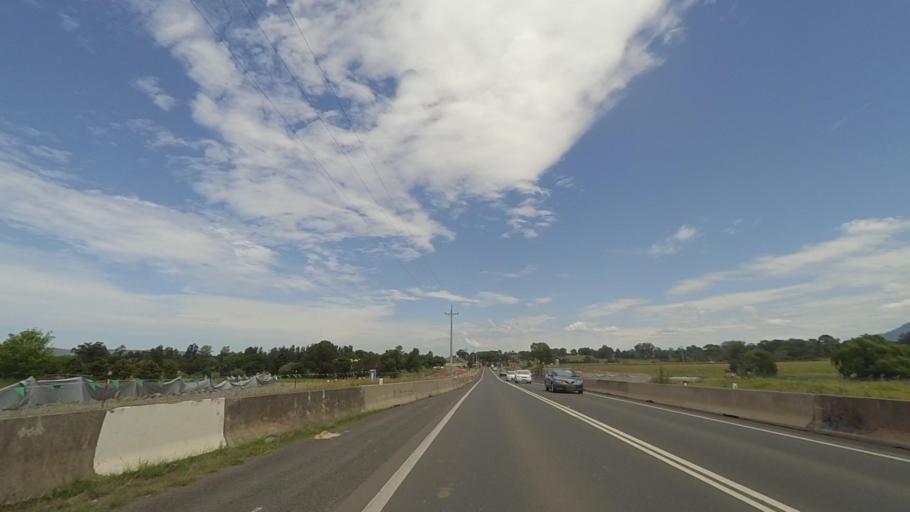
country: AU
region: New South Wales
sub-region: Shoalhaven Shire
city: Berry
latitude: -34.7851
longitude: 150.6766
